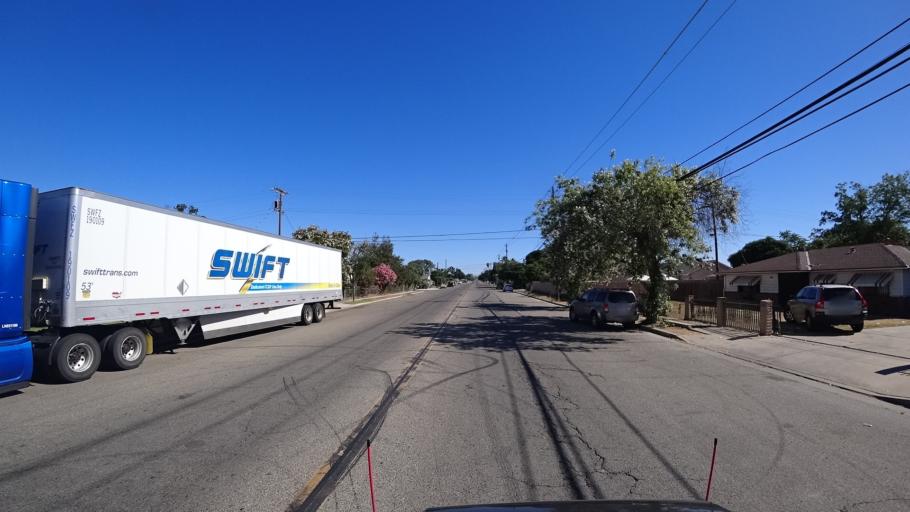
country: US
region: California
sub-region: Fresno County
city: West Park
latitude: 36.7079
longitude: -119.8089
